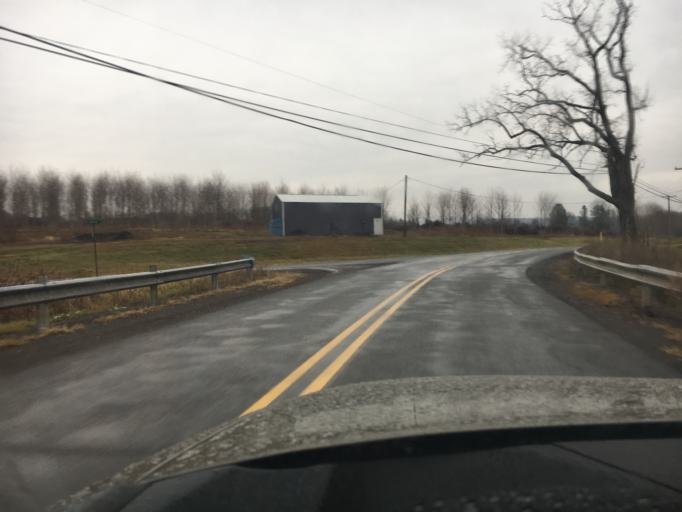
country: US
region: Pennsylvania
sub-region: Luzerne County
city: Conyngham
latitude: 41.0287
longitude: -76.0162
